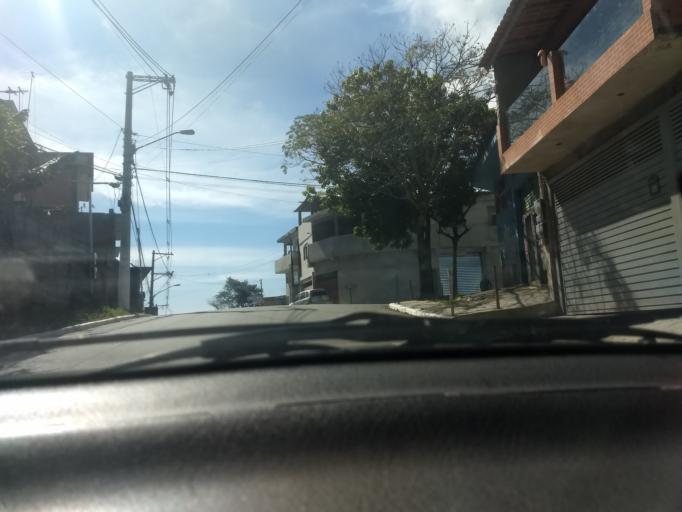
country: BR
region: Sao Paulo
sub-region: Embu-Guacu
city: Embu Guacu
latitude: -23.8211
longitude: -46.7062
